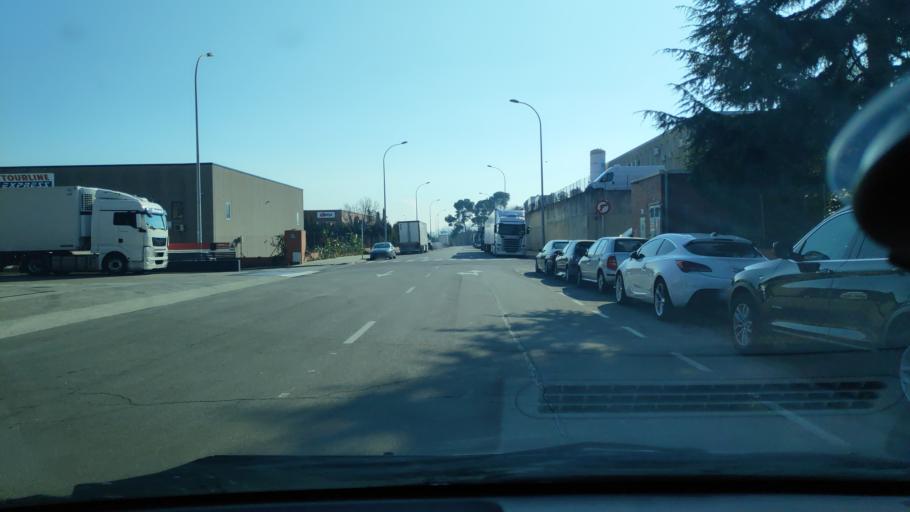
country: ES
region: Catalonia
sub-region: Provincia de Barcelona
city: Sant Quirze del Valles
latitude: 41.5217
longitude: 2.0927
